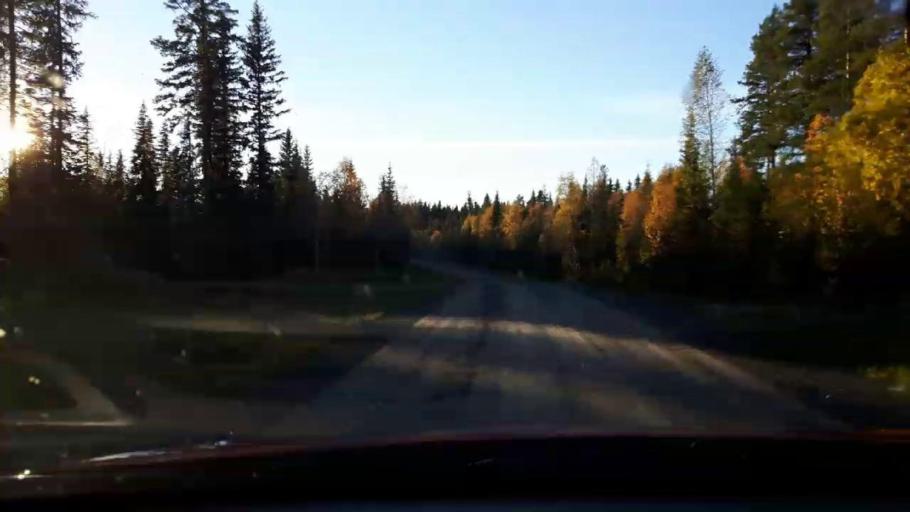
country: SE
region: Jaemtland
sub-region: OEstersunds Kommun
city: Lit
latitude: 63.4135
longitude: 14.7090
